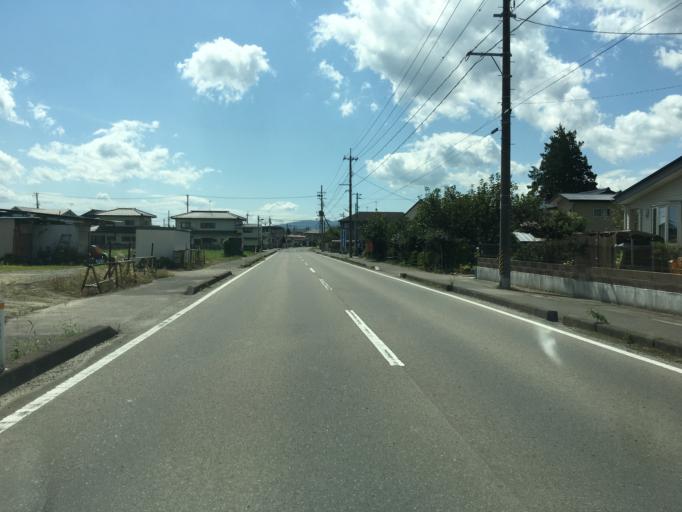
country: JP
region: Fukushima
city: Fukushima-shi
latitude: 37.7758
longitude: 140.4248
